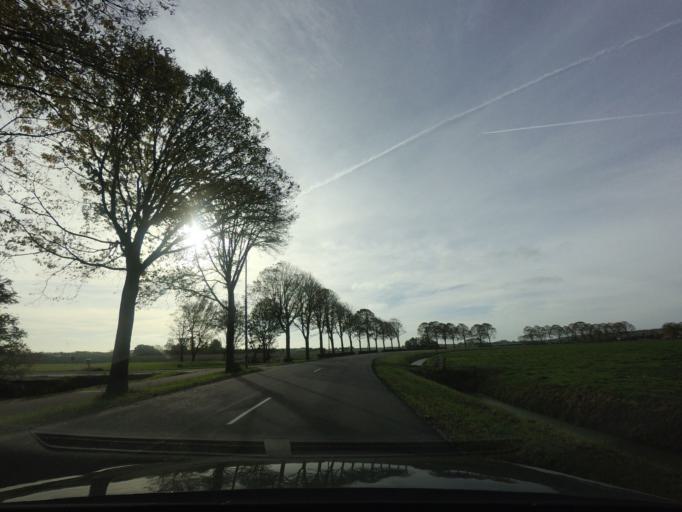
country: NL
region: North Holland
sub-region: Gemeente Schagen
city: Harenkarspel
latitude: 52.7106
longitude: 4.7277
